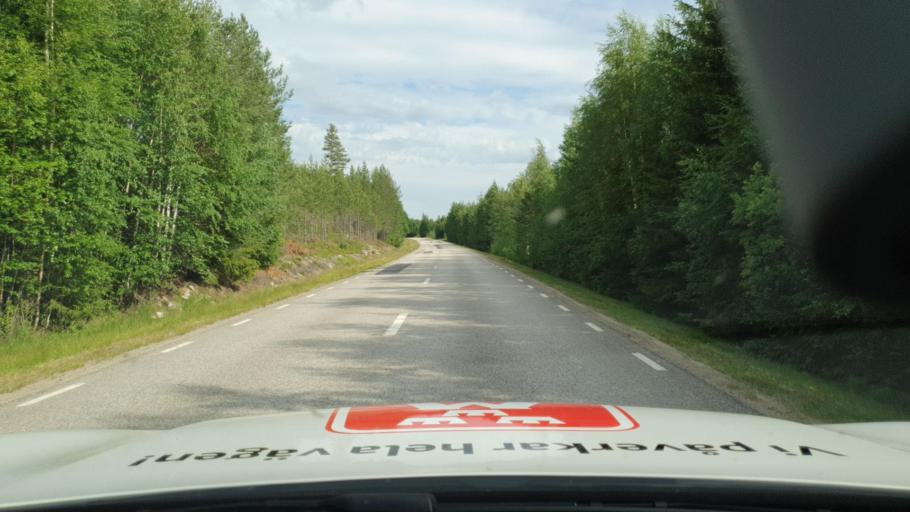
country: NO
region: Hedmark
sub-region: Trysil
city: Innbygda
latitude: 60.9352
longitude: 12.4857
